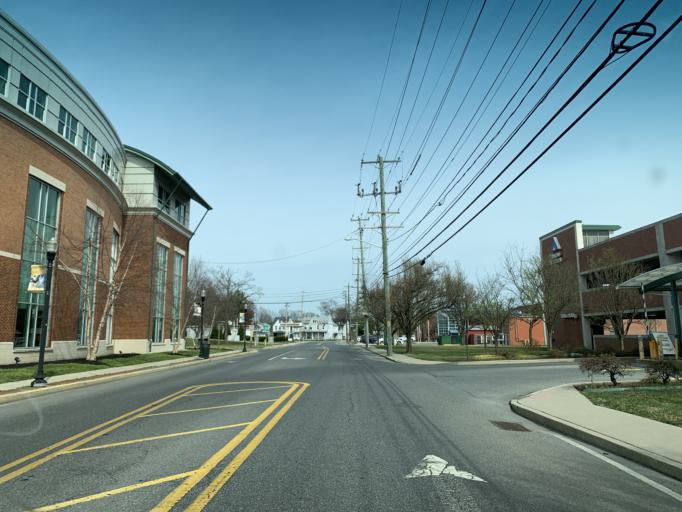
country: US
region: Maryland
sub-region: Cecil County
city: Elkton
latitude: 39.6106
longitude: -75.8324
